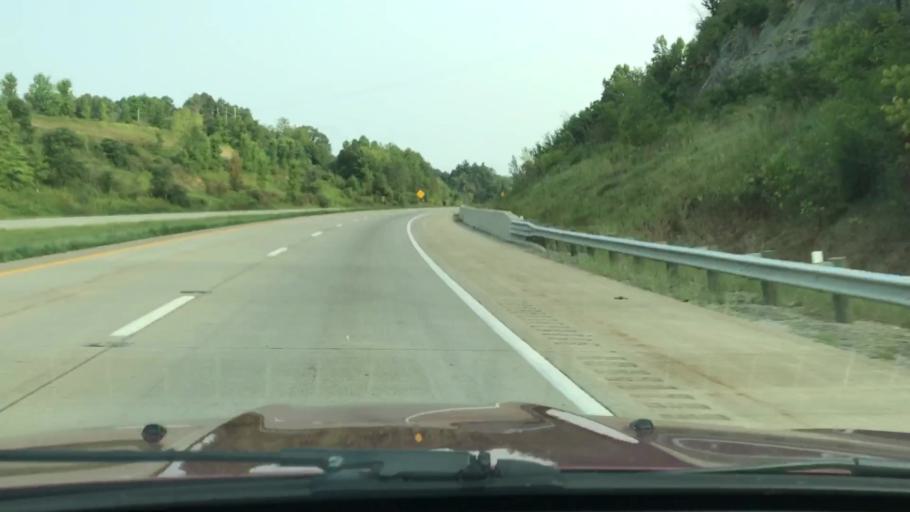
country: US
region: Ohio
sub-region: Noble County
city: Caldwell
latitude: 39.7803
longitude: -81.5531
